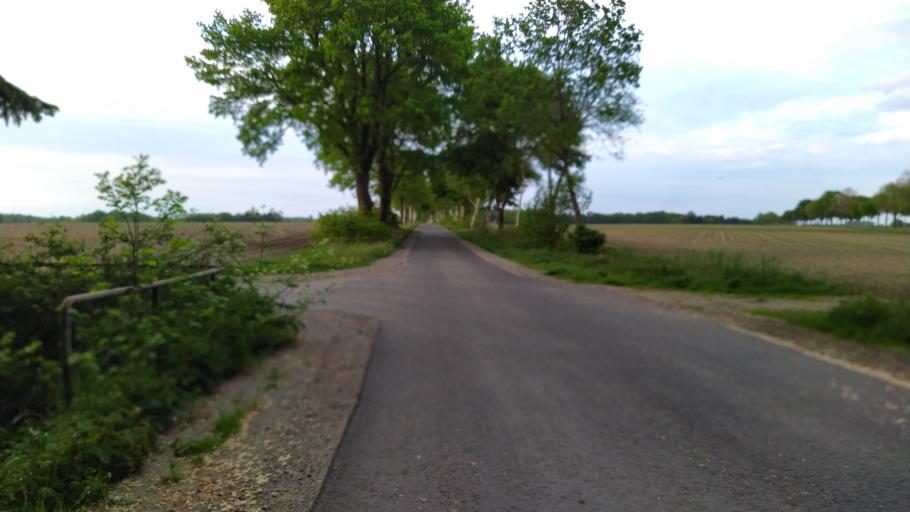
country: DE
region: Lower Saxony
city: Ahlerstedt
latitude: 53.4074
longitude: 9.4130
